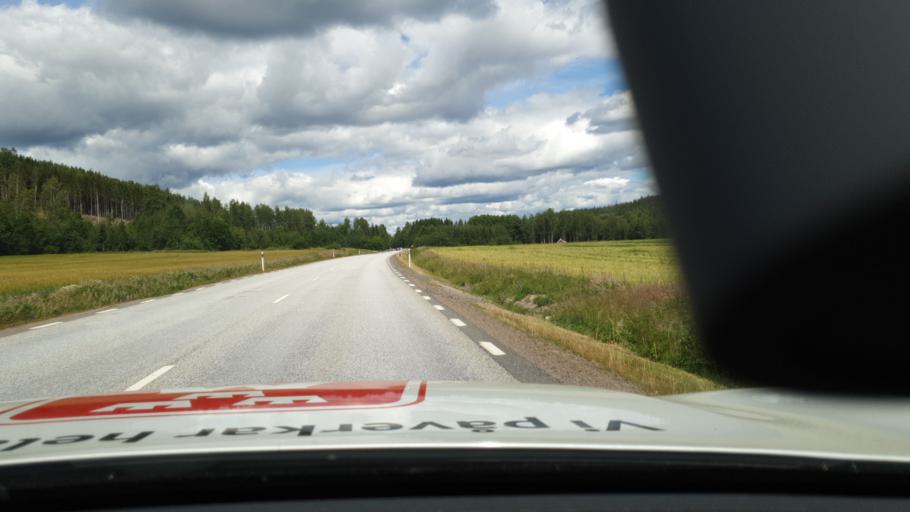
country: SE
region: Vaermland
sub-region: Storfors Kommun
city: Storfors
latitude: 59.5147
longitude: 14.3027
